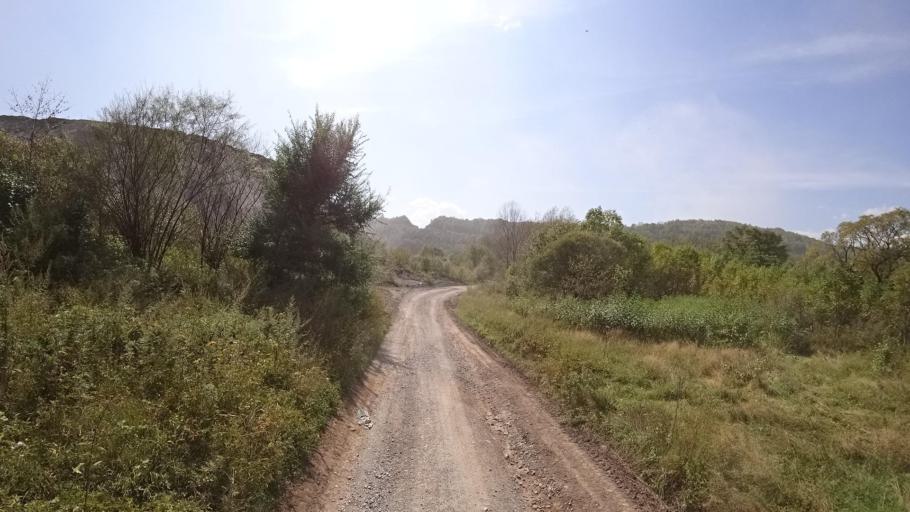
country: RU
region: Jewish Autonomous Oblast
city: Londoko
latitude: 49.0213
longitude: 131.9337
